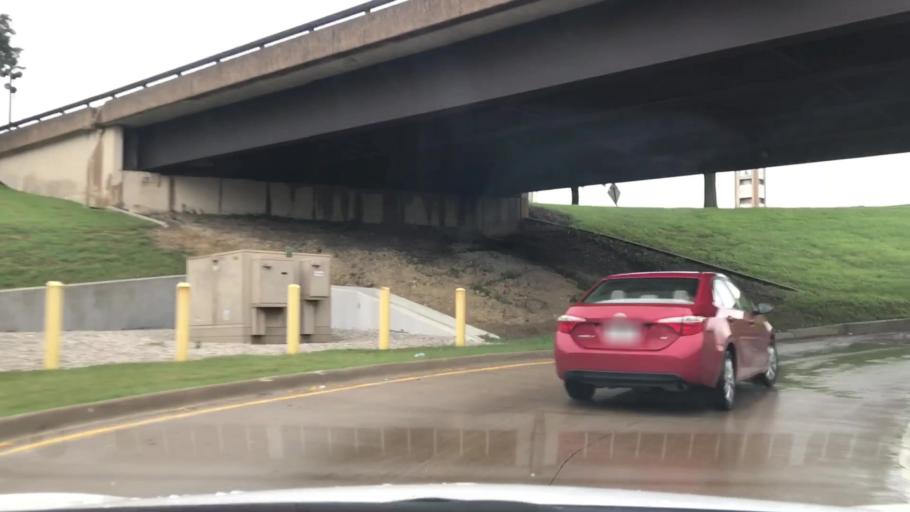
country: US
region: Texas
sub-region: Tarrant County
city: Grapevine
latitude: 32.9037
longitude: -97.0391
